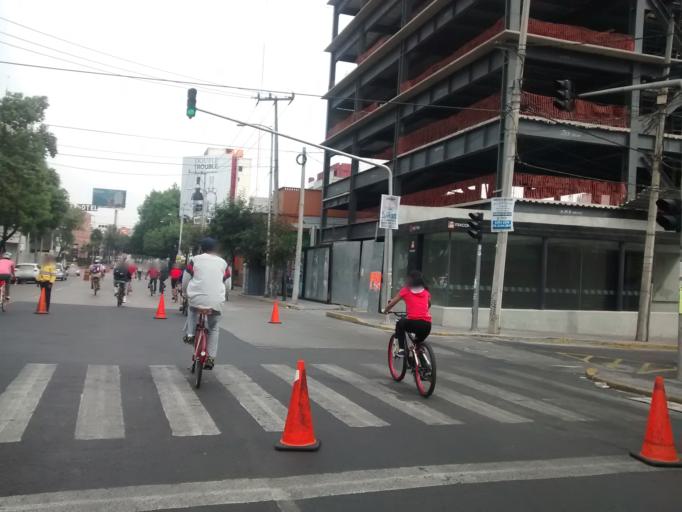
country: MX
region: Mexico City
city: Alvaro Obregon
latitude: 19.3760
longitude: -99.1866
